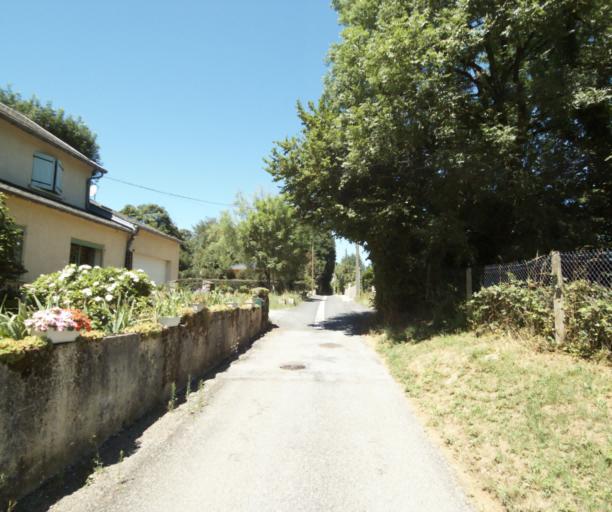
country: FR
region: Midi-Pyrenees
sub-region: Departement du Tarn
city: Dourgne
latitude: 43.4286
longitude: 2.1695
